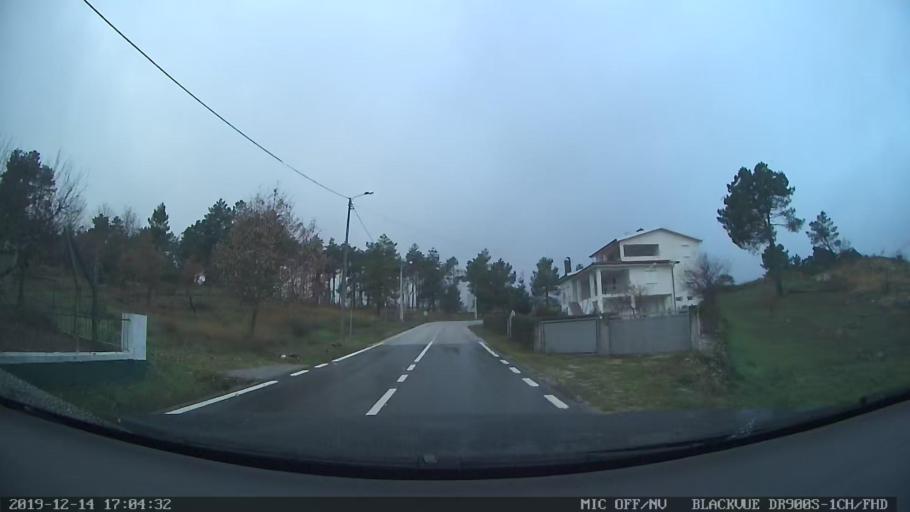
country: PT
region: Vila Real
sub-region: Vila Pouca de Aguiar
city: Vila Pouca de Aguiar
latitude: 41.4473
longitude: -7.5754
